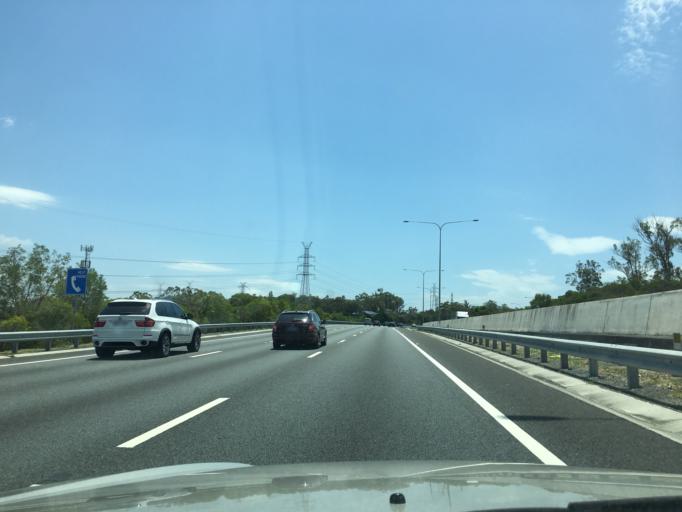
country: AU
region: Queensland
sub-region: Brisbane
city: Mackenzie
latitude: -27.5443
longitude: 153.1172
